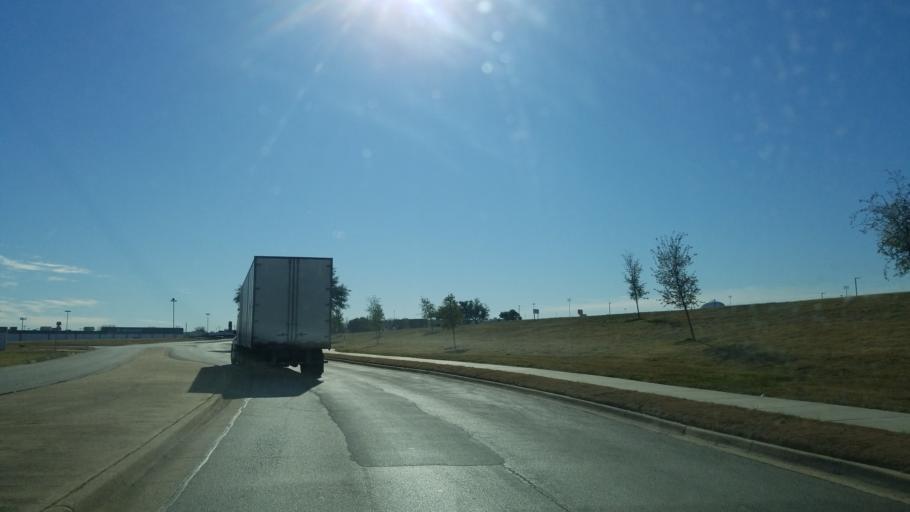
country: US
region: Texas
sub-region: Tarrant County
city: Arlington
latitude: 32.7454
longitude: -97.0541
